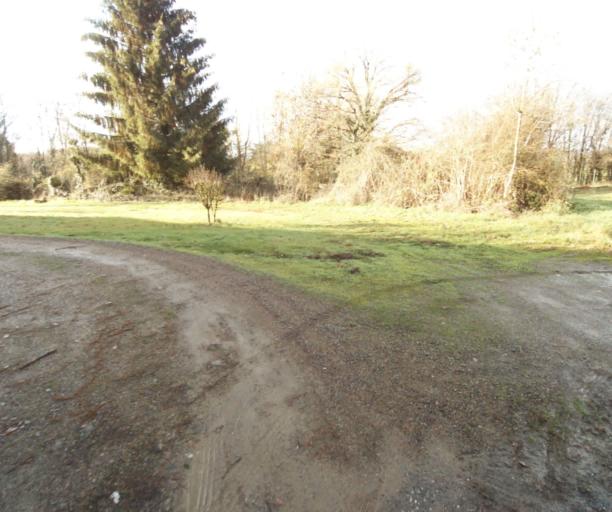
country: FR
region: Limousin
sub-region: Departement de la Correze
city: Sainte-Fereole
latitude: 45.2463
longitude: 1.6092
